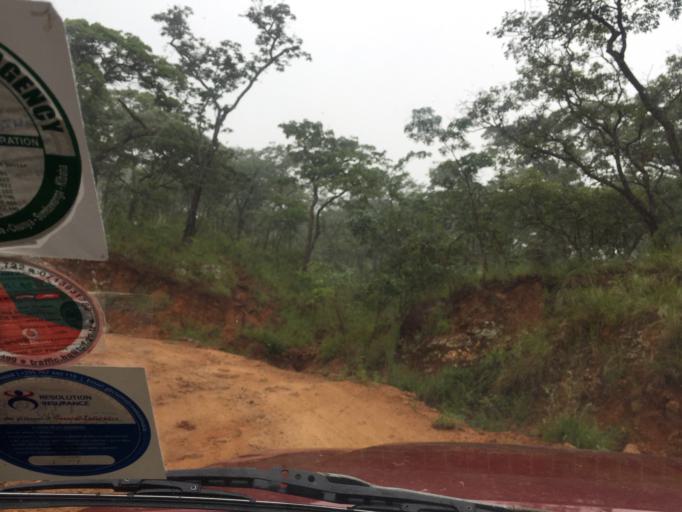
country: TZ
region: Mbeya
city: Chimala
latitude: -8.8708
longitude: 33.9943
